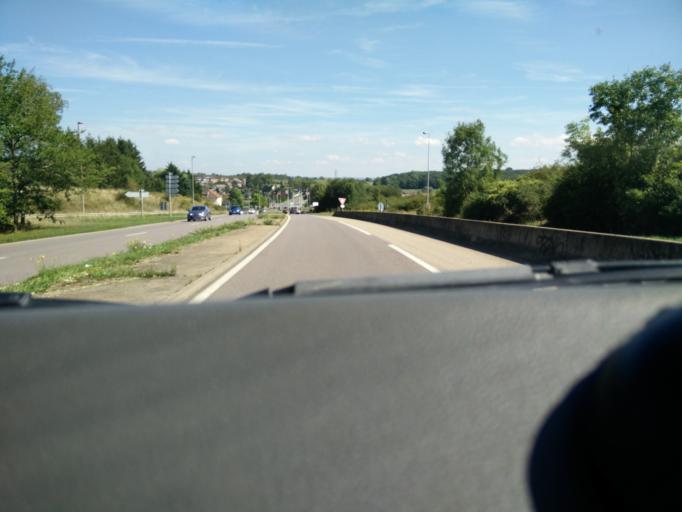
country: FR
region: Lorraine
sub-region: Departement de la Moselle
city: Terville
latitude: 49.3637
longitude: 6.1079
